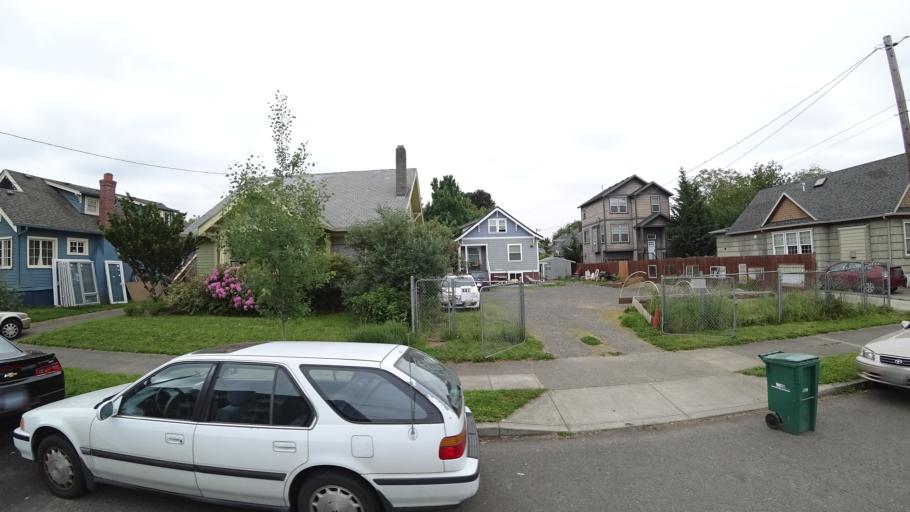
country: US
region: Oregon
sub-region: Multnomah County
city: Portland
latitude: 45.5455
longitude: -122.6606
